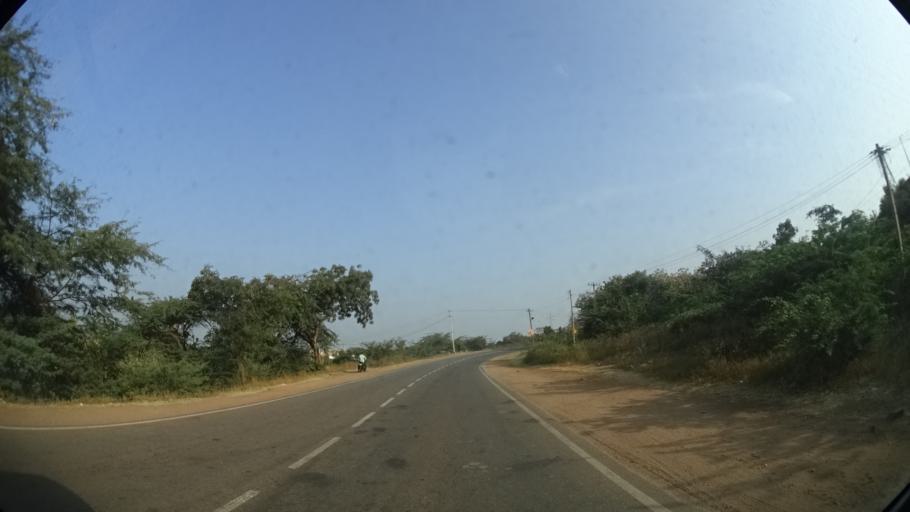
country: IN
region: Karnataka
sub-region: Bellary
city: Hospet
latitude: 15.2543
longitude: 76.3730
